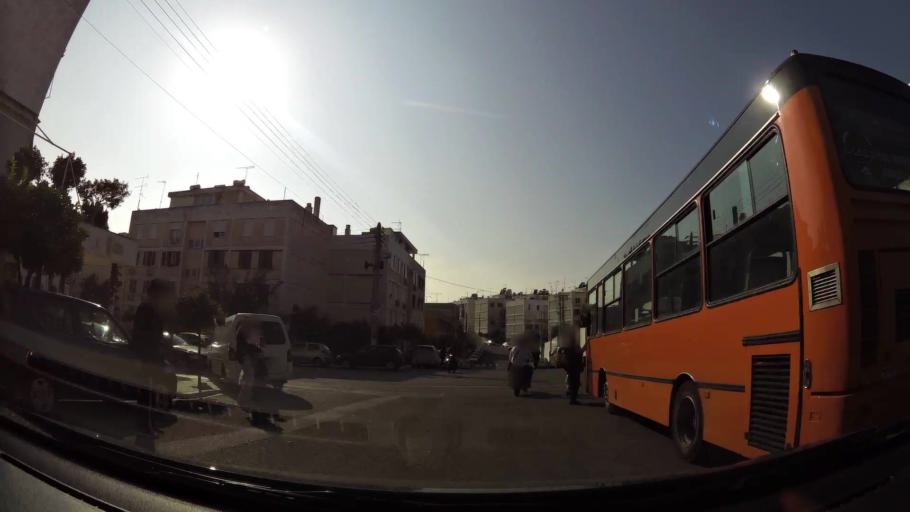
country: GR
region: Attica
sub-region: Nomos Attikis
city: Piraeus
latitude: 37.9479
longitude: 23.6307
